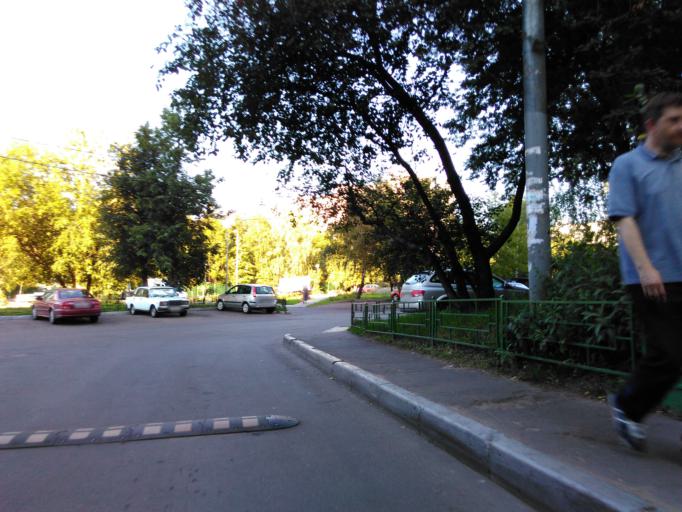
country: RU
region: Moscow
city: Tyoply Stan
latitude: 55.6311
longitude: 37.5097
